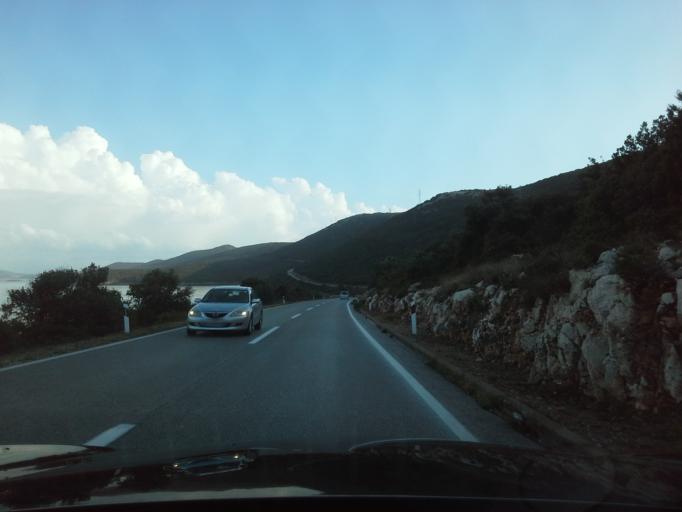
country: HR
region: Primorsko-Goranska
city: Mali Losinj
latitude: 44.6331
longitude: 14.3923
